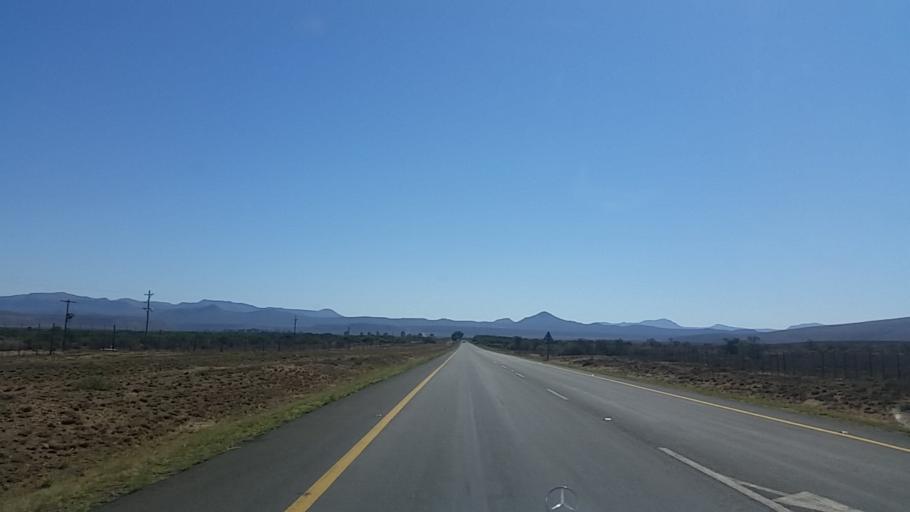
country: ZA
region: Eastern Cape
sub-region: Cacadu District Municipality
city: Graaff-Reinet
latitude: -32.2184
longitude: 24.5429
